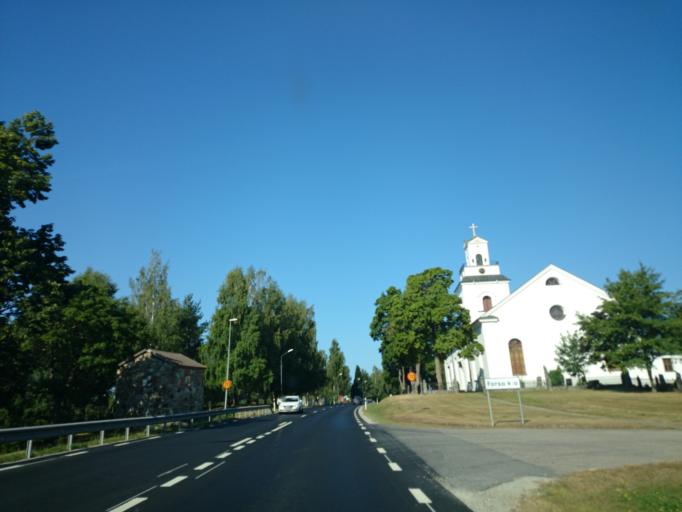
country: SE
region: Gaevleborg
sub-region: Hudiksvalls Kommun
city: Sorforsa
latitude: 61.7337
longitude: 16.9411
